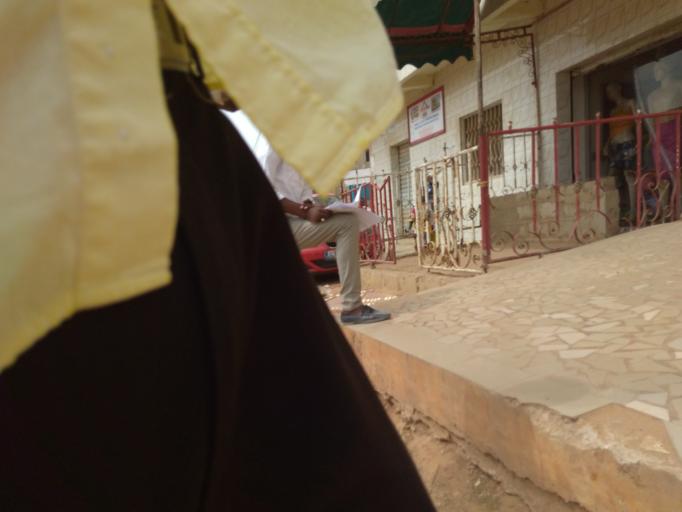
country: SN
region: Dakar
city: Pikine
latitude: 14.8005
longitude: -17.3376
